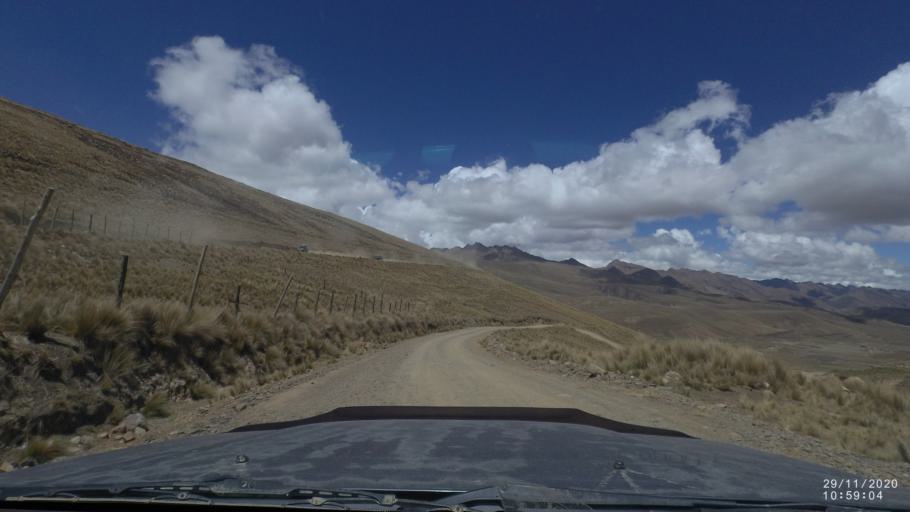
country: BO
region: Cochabamba
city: Cochabamba
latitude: -17.2082
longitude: -66.2262
